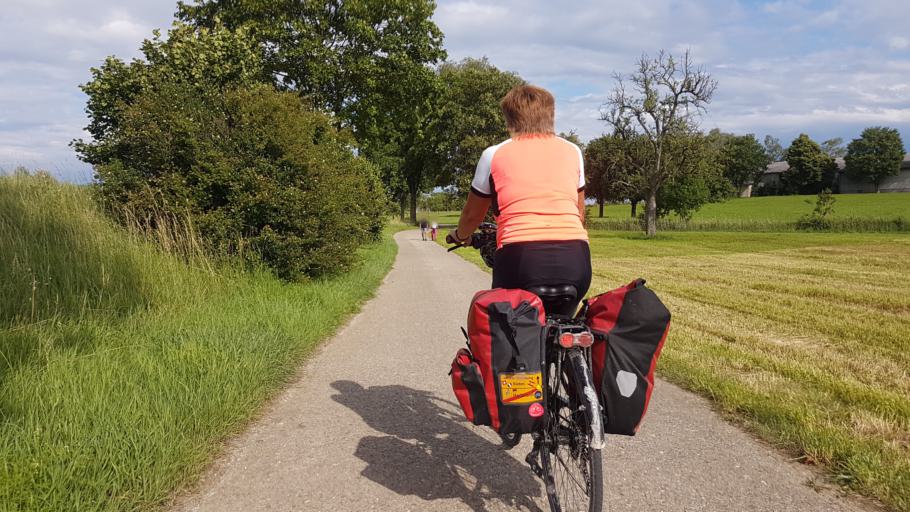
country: DE
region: Baden-Wuerttemberg
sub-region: Tuebingen Region
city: Rottenacker
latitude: 48.2304
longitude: 9.6721
